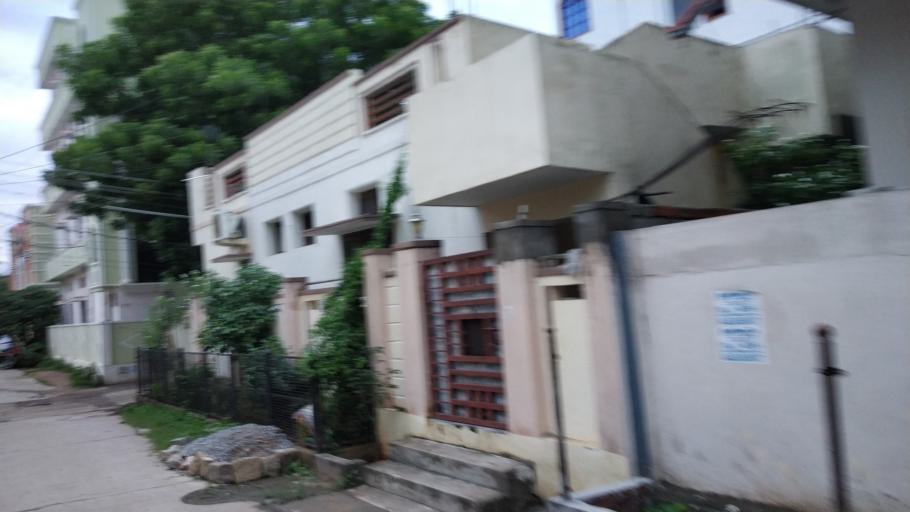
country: IN
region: Telangana
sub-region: Medak
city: Serilingampalle
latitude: 17.5104
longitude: 78.3052
